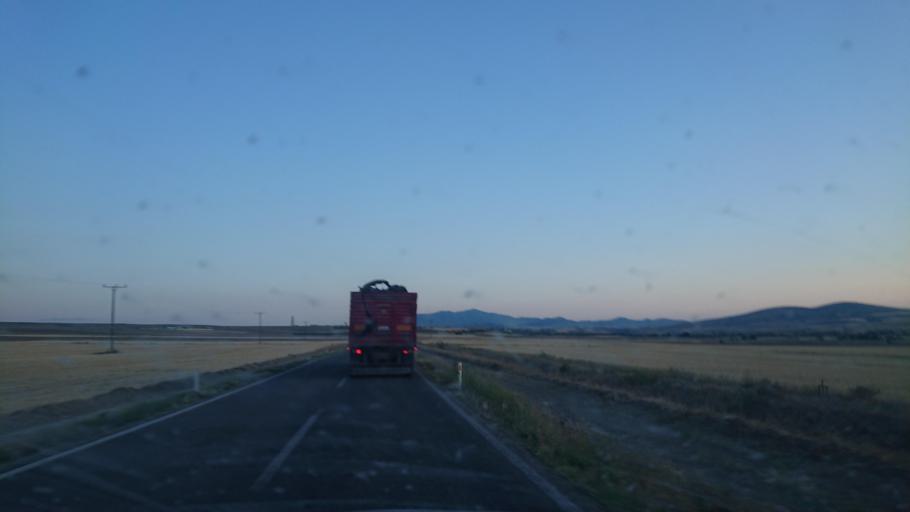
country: TR
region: Aksaray
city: Balci
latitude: 38.8153
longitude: 34.1342
